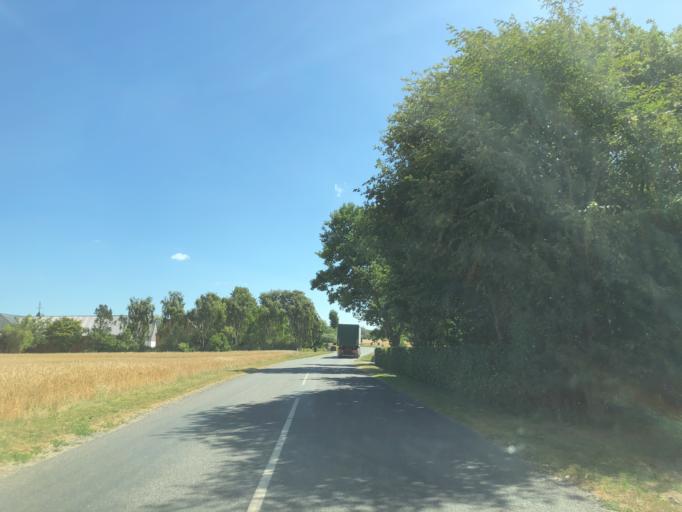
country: DK
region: North Denmark
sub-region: Vesthimmerland Kommune
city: Alestrup
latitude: 56.5839
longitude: 9.6118
